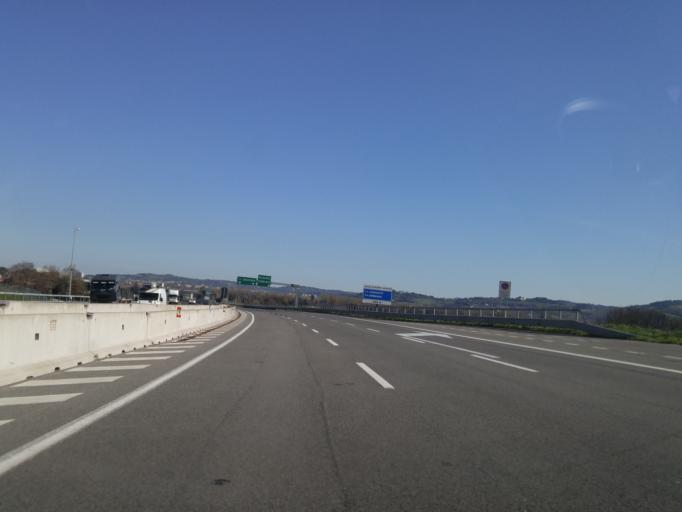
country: IT
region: The Marches
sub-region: Provincia di Pesaro e Urbino
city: Villa Ceccolini
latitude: 43.8992
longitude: 12.8369
